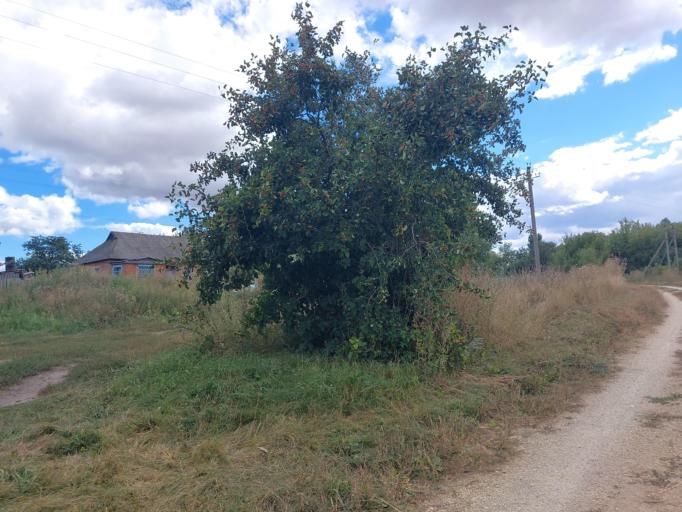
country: RU
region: Lipetsk
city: Terbuny
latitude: 52.2614
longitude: 38.2068
